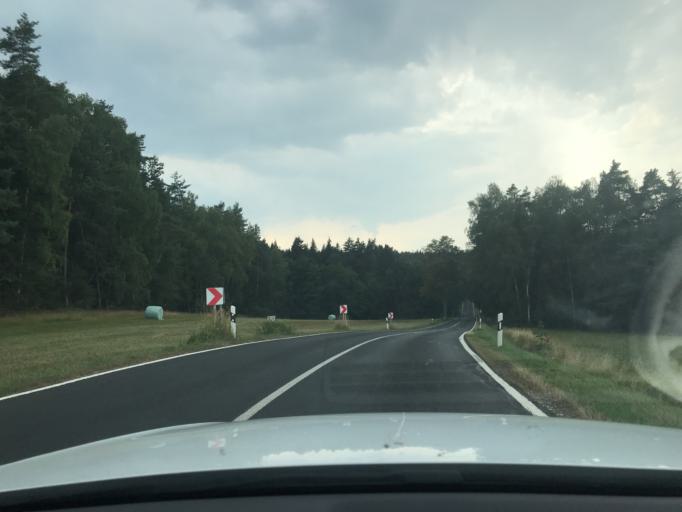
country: DE
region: Bavaria
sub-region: Upper Franconia
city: Prebitz
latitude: 49.7946
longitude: 11.6715
